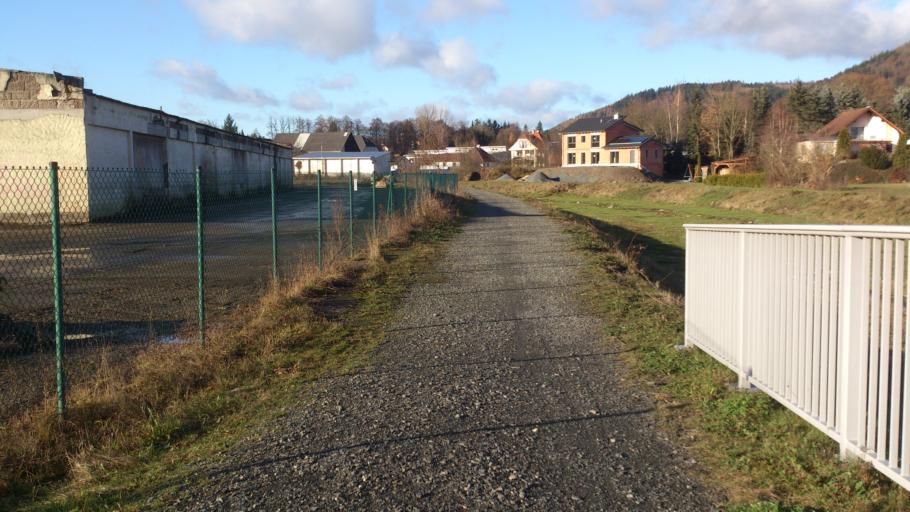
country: DE
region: Bavaria
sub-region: Upper Franconia
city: Stadtsteinach
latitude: 50.1622
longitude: 11.5096
